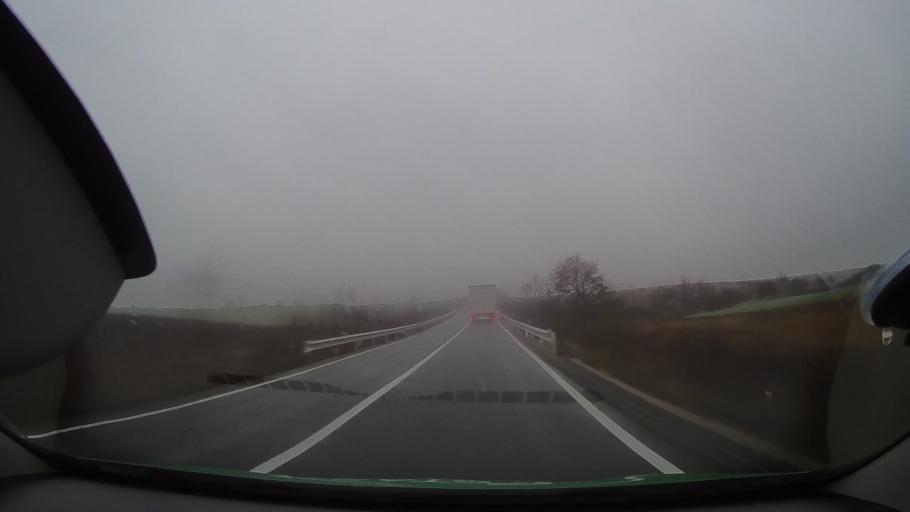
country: RO
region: Bihor
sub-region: Comuna Olcea
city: Olcea
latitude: 46.6722
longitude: 21.9646
